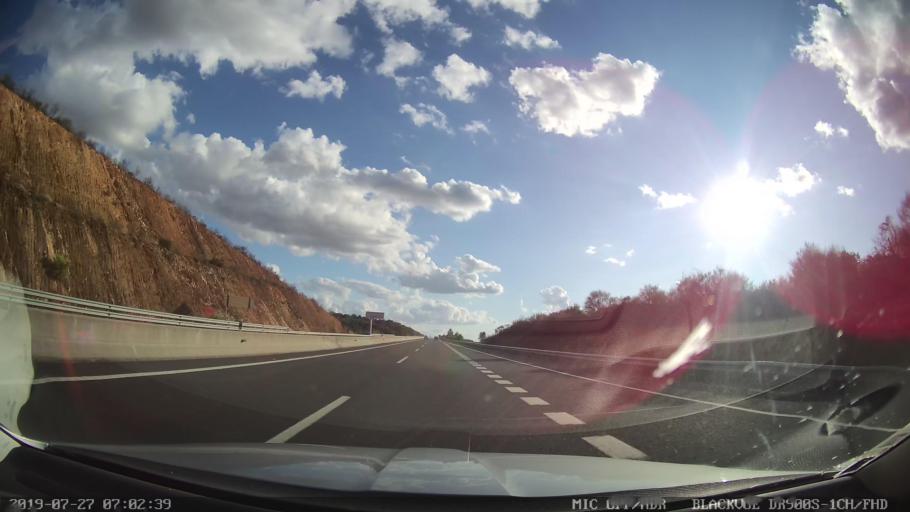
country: ES
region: Extremadura
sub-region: Provincia de Caceres
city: Casas de Miravete
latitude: 39.6851
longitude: -5.7237
